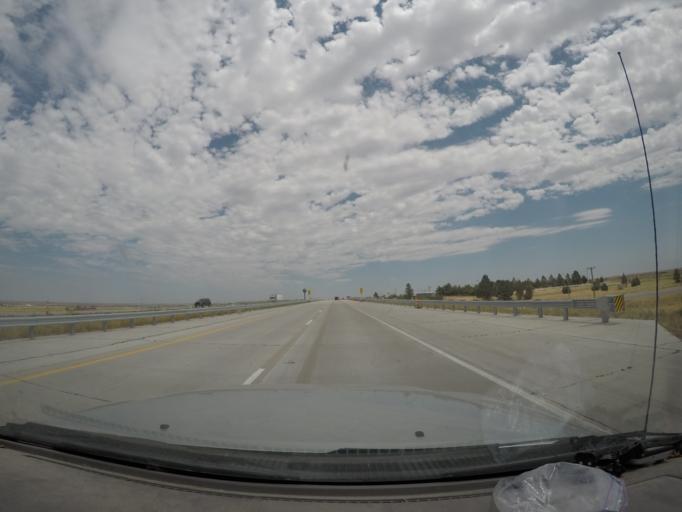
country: US
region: Nebraska
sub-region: Cheyenne County
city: Sidney
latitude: 41.1132
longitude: -102.9752
